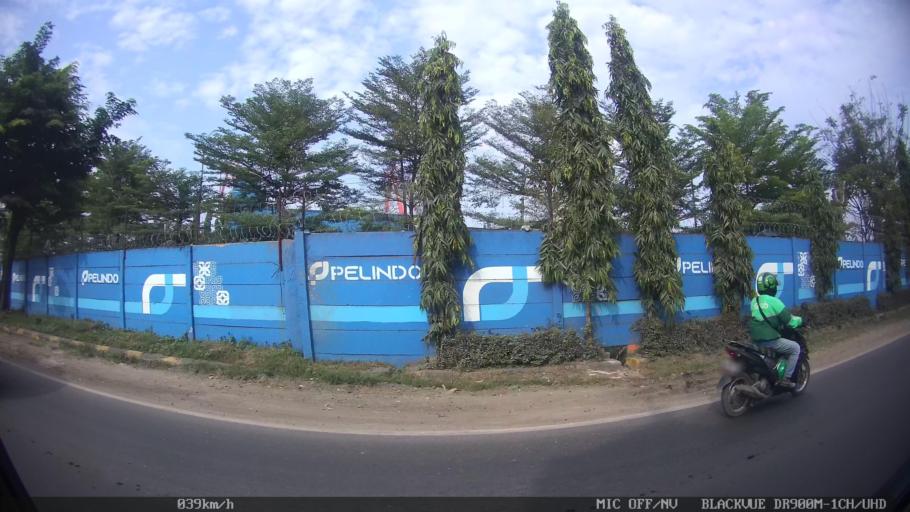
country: ID
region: Lampung
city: Panjang
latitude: -5.4676
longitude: 105.3209
